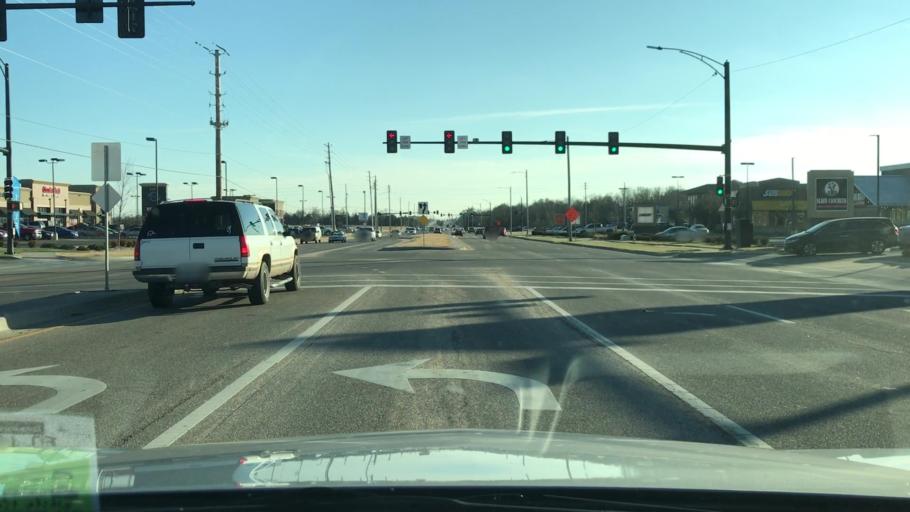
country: US
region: Kansas
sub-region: Sedgwick County
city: Bellaire
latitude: 37.7257
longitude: -97.2079
